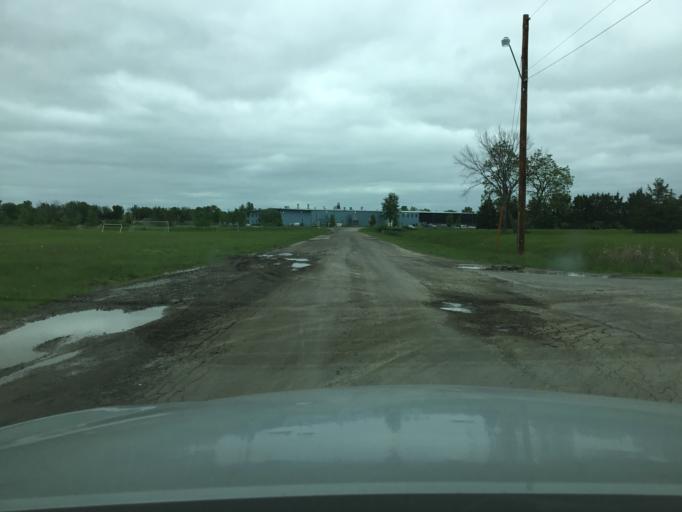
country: US
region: Kansas
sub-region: Franklin County
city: Ottawa
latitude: 38.6360
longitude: -95.2585
